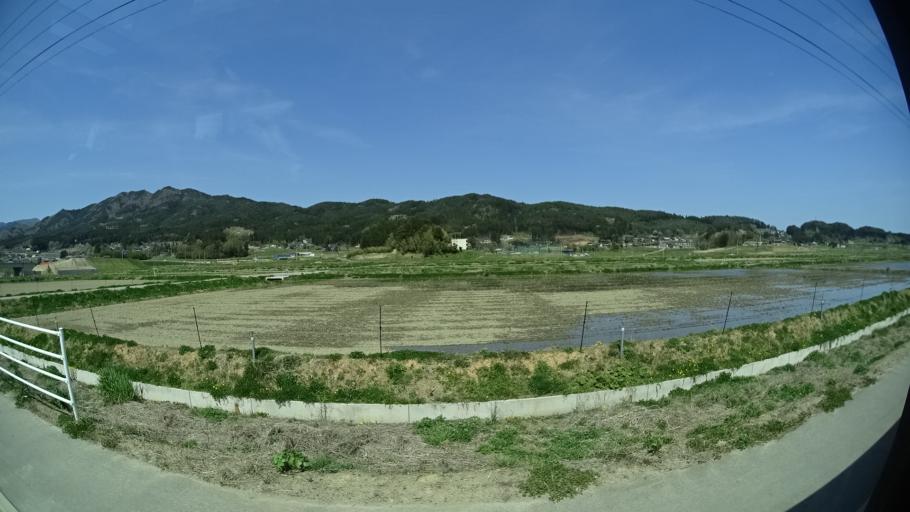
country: JP
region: Iwate
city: Ofunato
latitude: 38.9929
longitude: 141.6928
